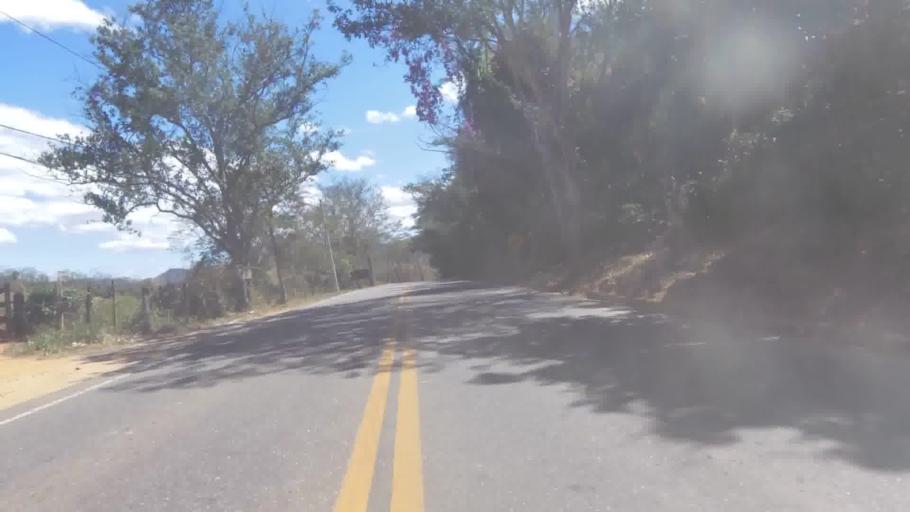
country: BR
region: Espirito Santo
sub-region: Cachoeiro De Itapemirim
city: Cachoeiro de Itapemirim
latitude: -20.9079
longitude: -41.2013
